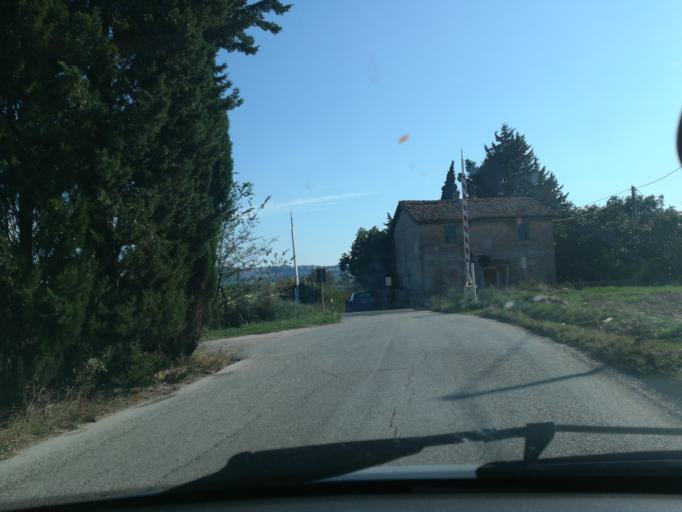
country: IT
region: The Marches
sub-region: Provincia di Macerata
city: Piediripa
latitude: 43.2864
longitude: 13.4881
